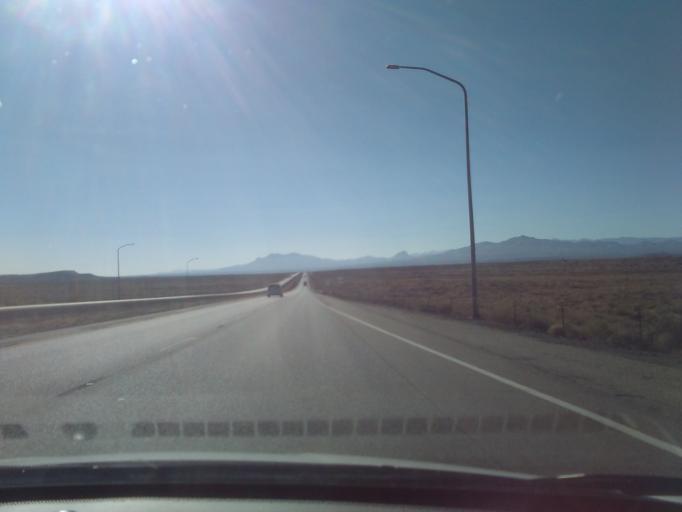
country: US
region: New Mexico
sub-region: Socorro County
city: Socorro
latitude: 34.3031
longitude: -106.8908
